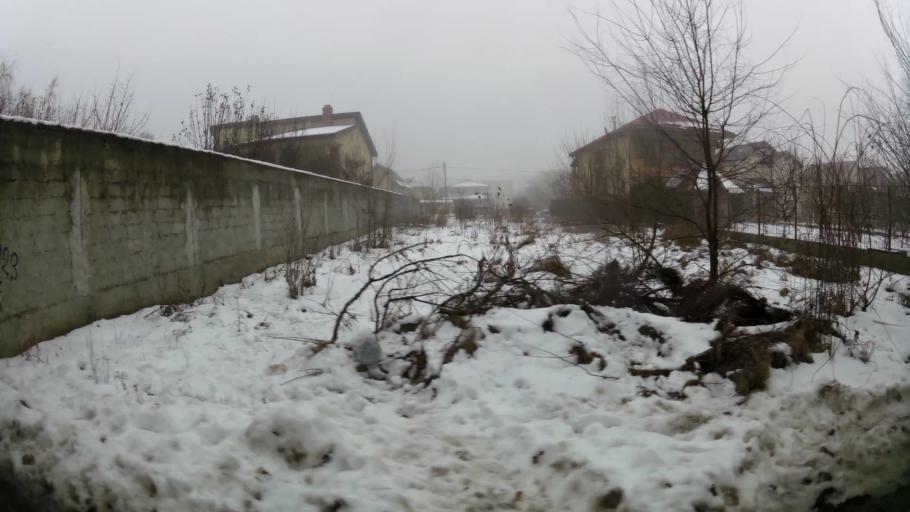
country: RO
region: Ilfov
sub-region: Comuna Chiajna
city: Rosu
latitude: 44.4559
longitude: 25.9984
